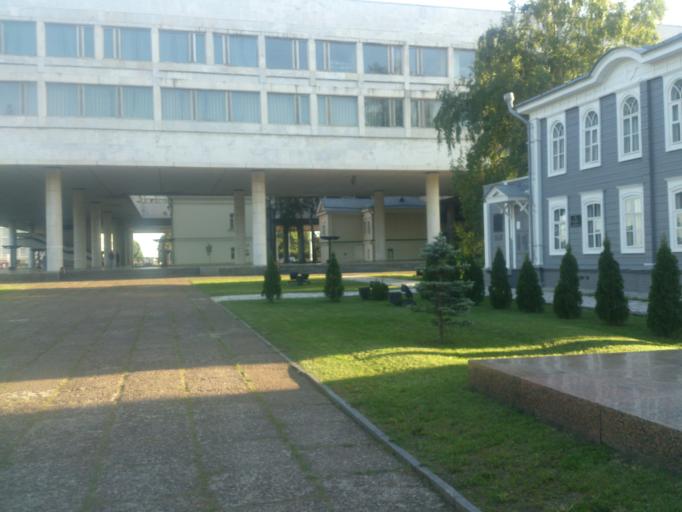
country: RU
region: Ulyanovsk
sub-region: Ulyanovskiy Rayon
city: Ulyanovsk
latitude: 54.3206
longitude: 48.4072
